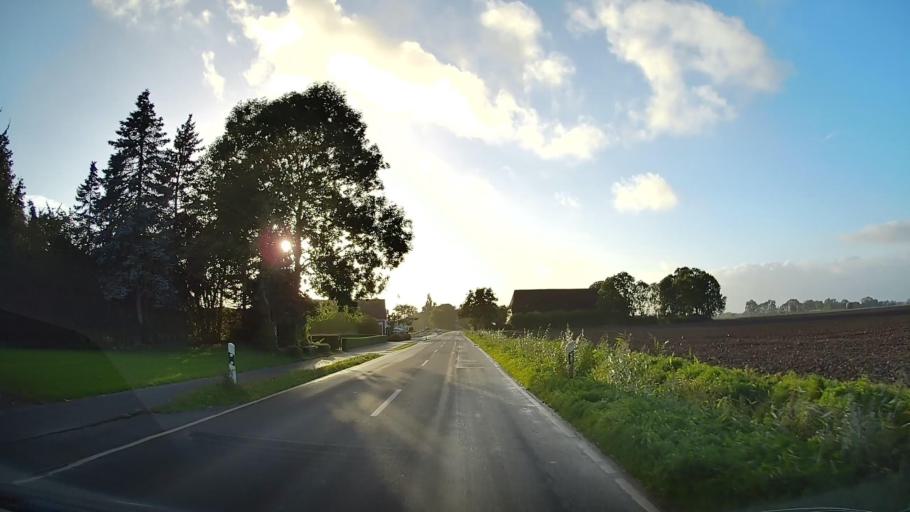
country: DE
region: Schleswig-Holstein
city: Herzhorn
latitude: 53.7891
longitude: 9.4601
